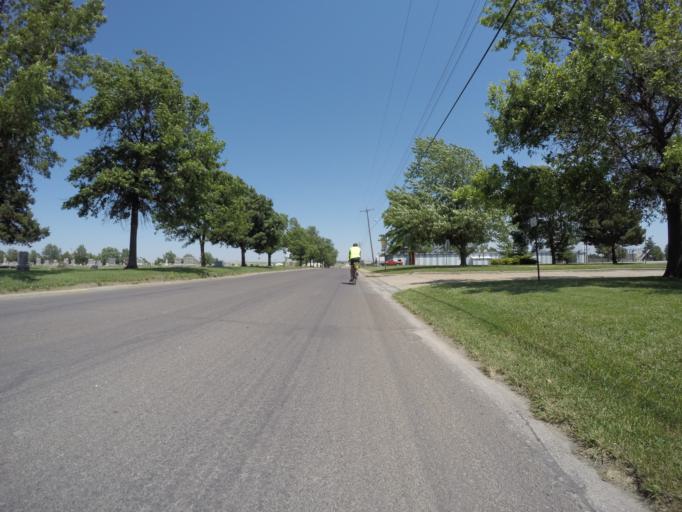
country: US
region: Kansas
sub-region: Nemaha County
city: Sabetha
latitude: 39.8997
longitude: -95.7912
